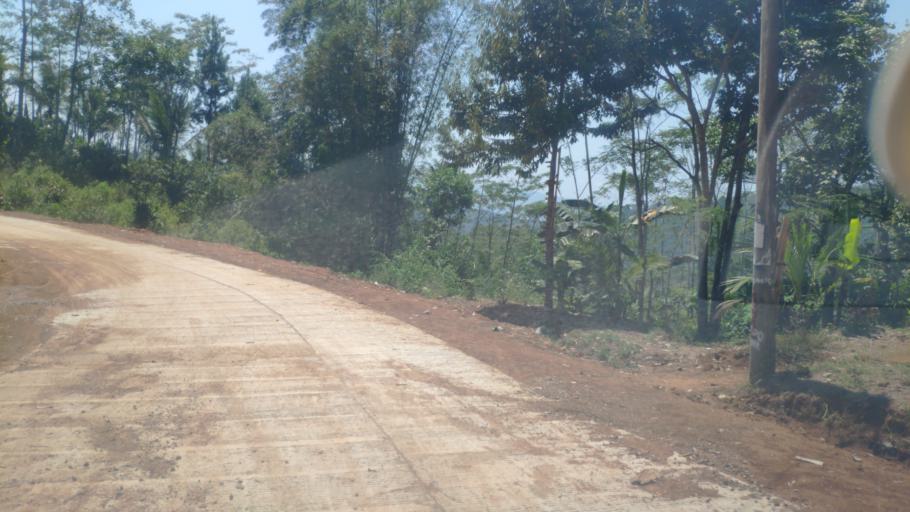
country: ID
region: Central Java
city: Buaran
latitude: -7.3002
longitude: 109.6323
